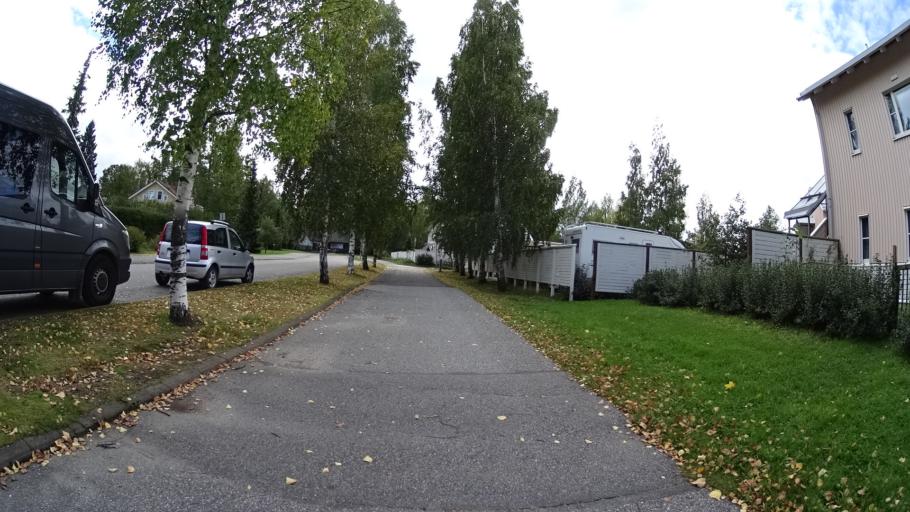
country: FI
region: Uusimaa
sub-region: Helsinki
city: Vantaa
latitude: 60.2635
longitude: 24.9526
